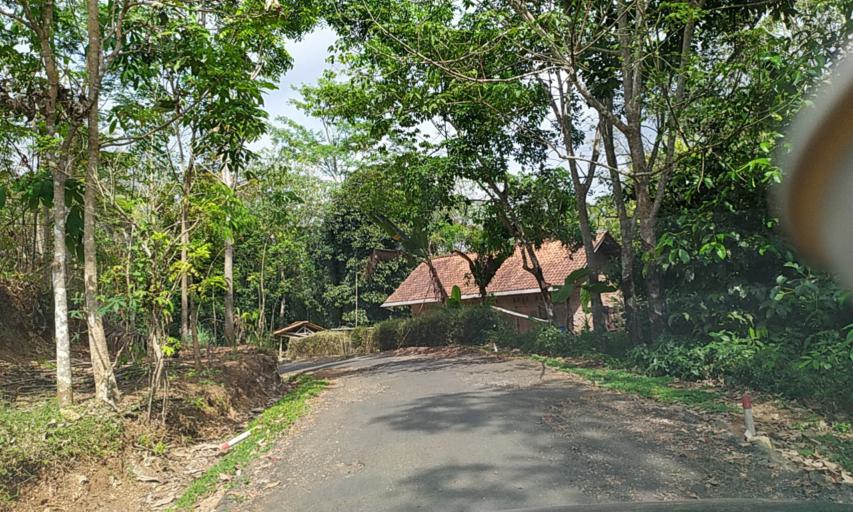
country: ID
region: Central Java
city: Cirateun
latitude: -7.2850
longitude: 108.5841
